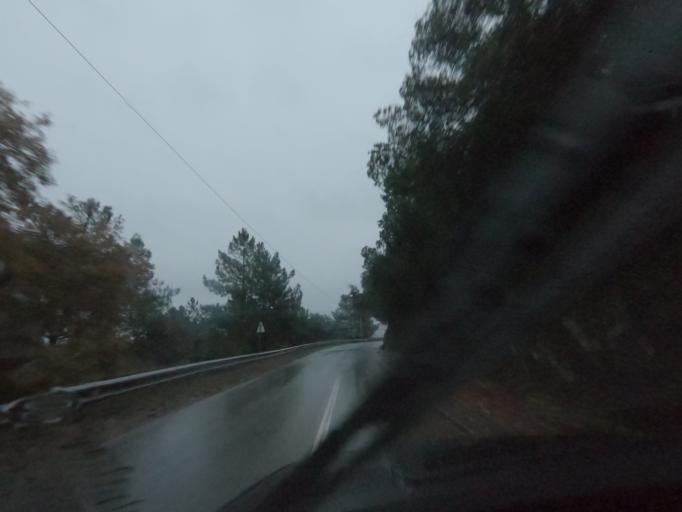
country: PT
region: Vila Real
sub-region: Sabrosa
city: Vilela
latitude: 41.2196
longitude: -7.5551
